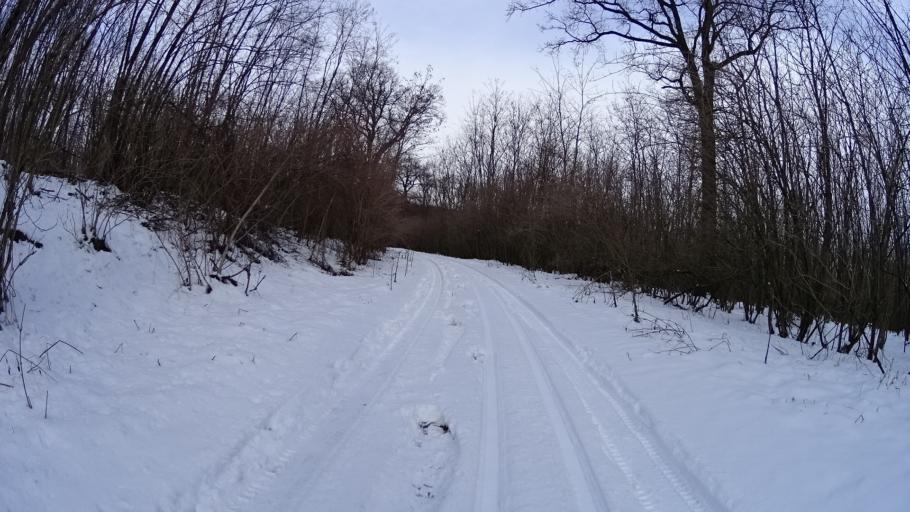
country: AT
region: Lower Austria
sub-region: Politischer Bezirk Korneuburg
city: Leobendorf
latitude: 48.4056
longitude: 16.3309
